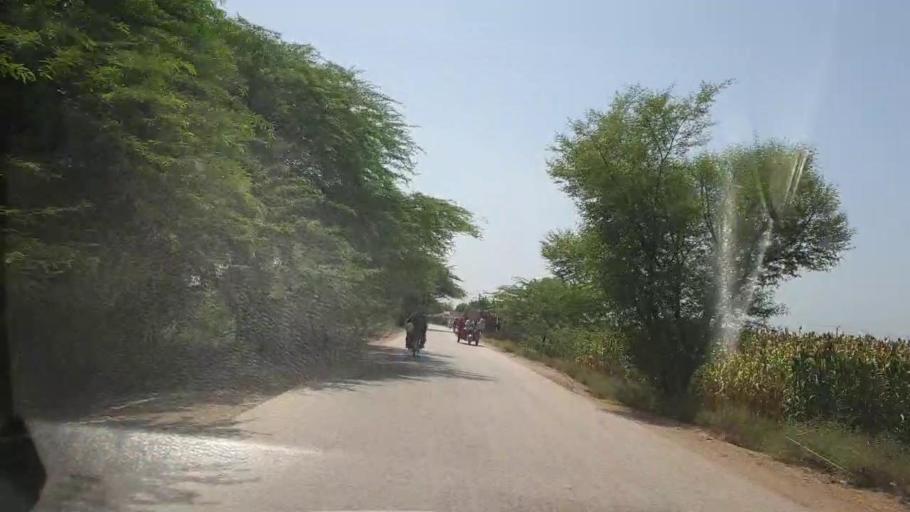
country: PK
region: Sindh
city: Bozdar
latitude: 27.0731
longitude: 68.5996
